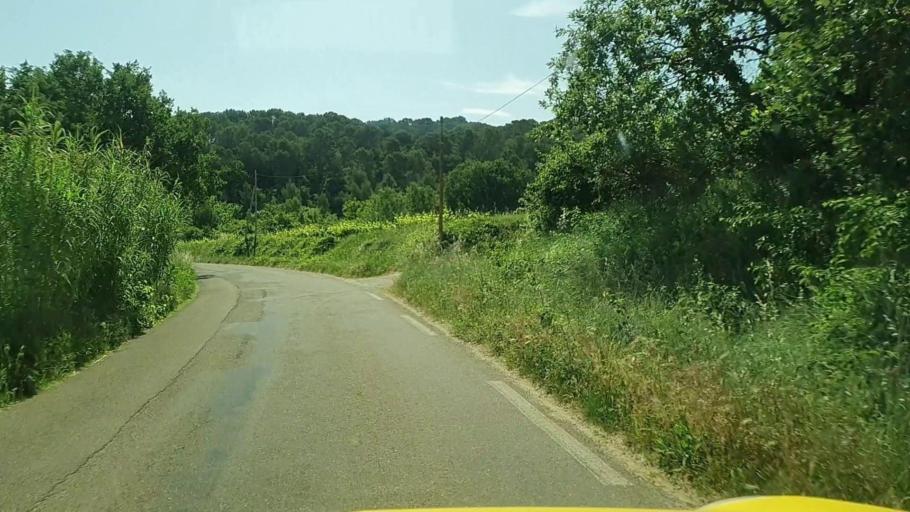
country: FR
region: Languedoc-Roussillon
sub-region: Departement du Gard
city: Connaux
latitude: 44.0910
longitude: 4.5820
